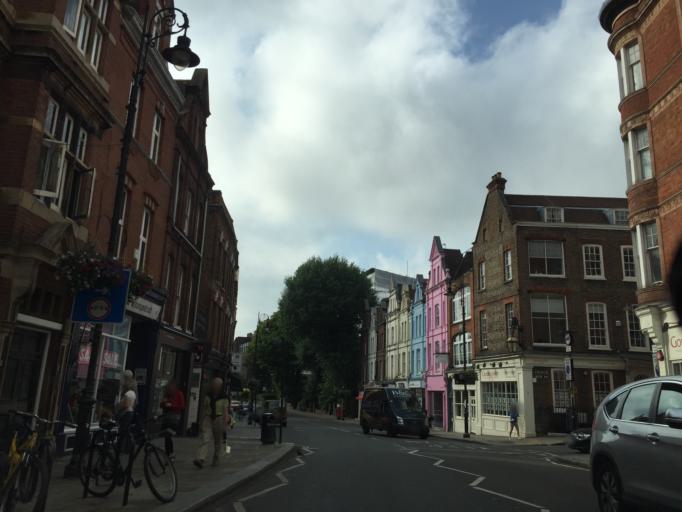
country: GB
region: England
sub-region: Greater London
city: Belsize Park
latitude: 51.5559
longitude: -0.1787
